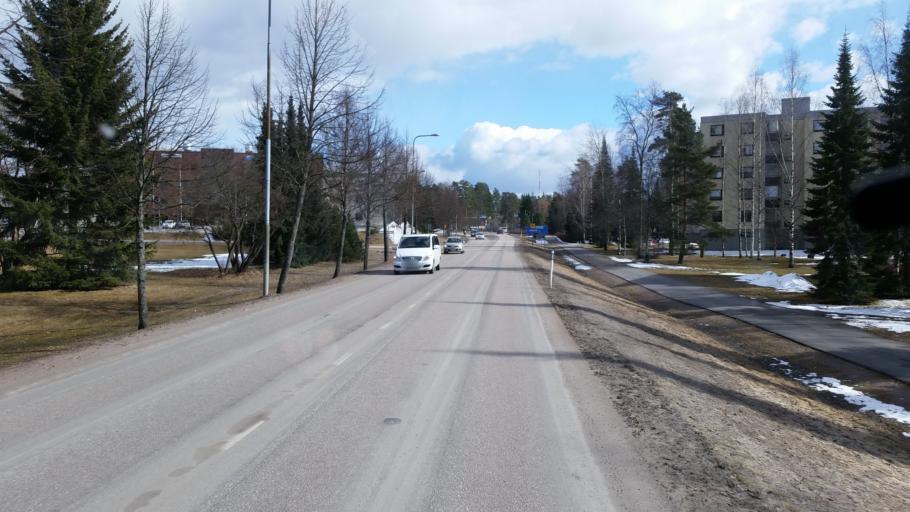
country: FI
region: South Karelia
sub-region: Imatra
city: Imatra
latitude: 61.1703
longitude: 28.7607
